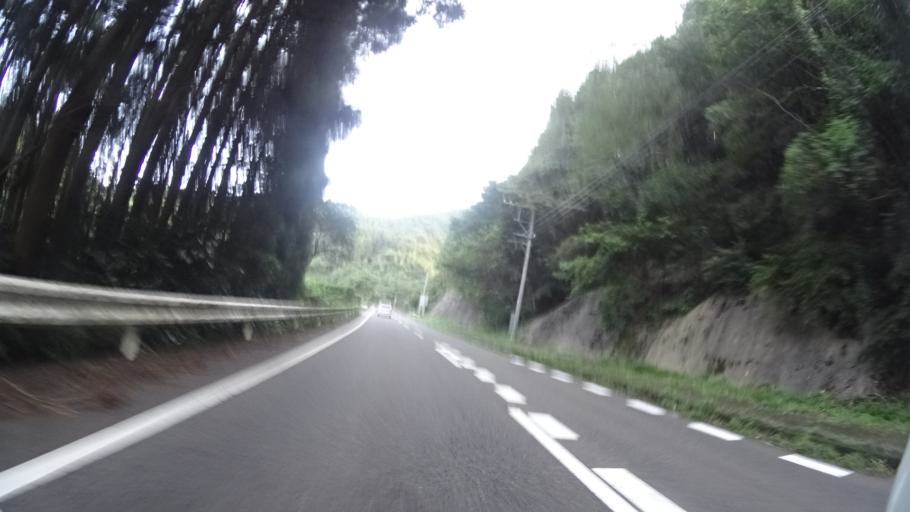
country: JP
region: Oita
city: Beppu
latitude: 33.3386
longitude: 131.3987
